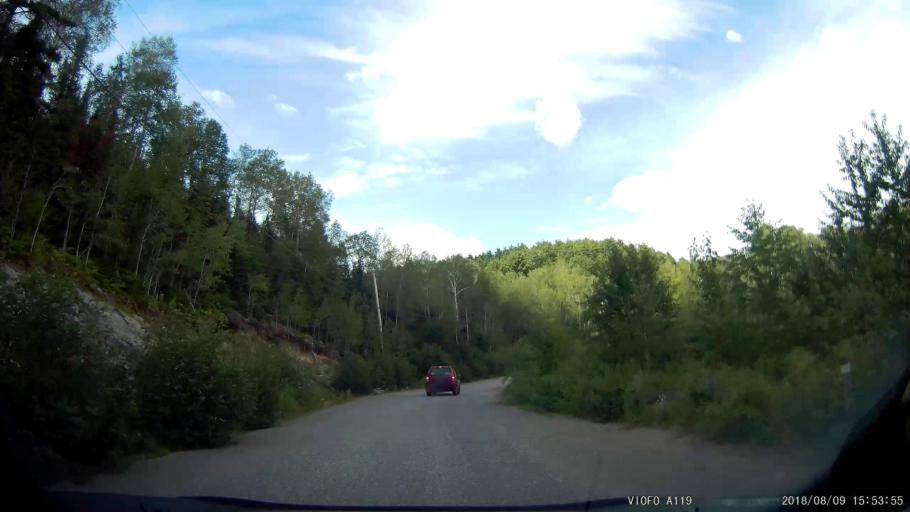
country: CA
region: Ontario
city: Rayside-Balfour
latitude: 46.6076
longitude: -81.5333
